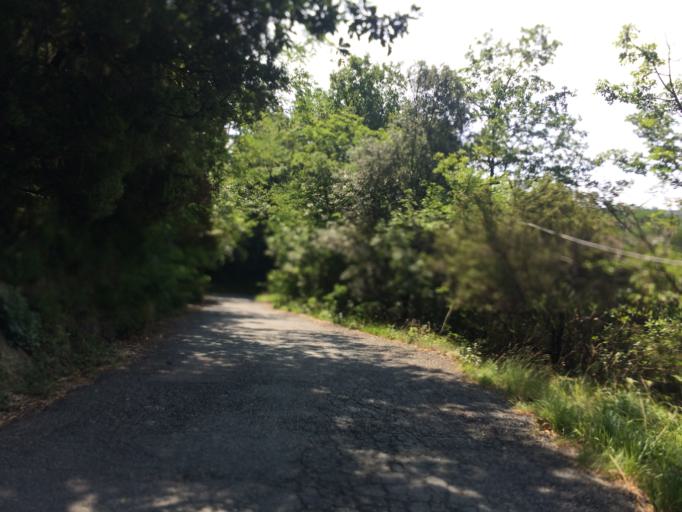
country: IT
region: Liguria
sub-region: Provincia di Genova
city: Sciarborasca
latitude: 44.4043
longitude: 8.5770
